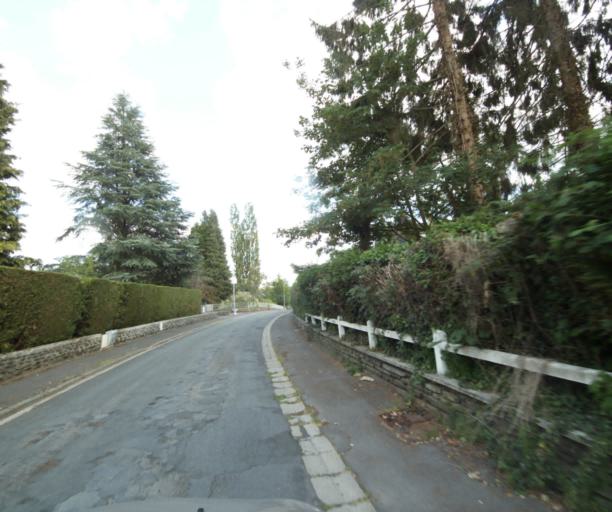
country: FR
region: Champagne-Ardenne
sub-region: Departement des Ardennes
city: Montcy-Notre-Dame
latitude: 49.7937
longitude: 4.7286
